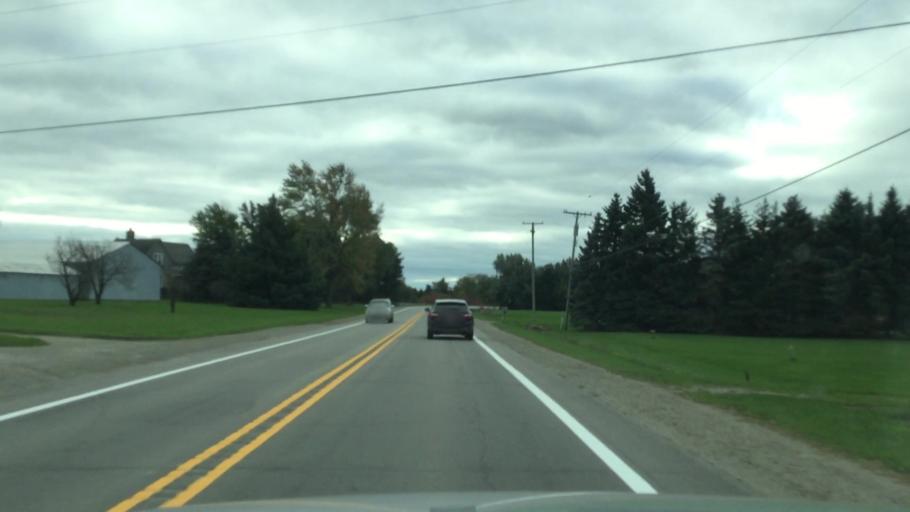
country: US
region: Michigan
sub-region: Macomb County
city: Memphis
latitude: 42.8573
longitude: -82.7655
